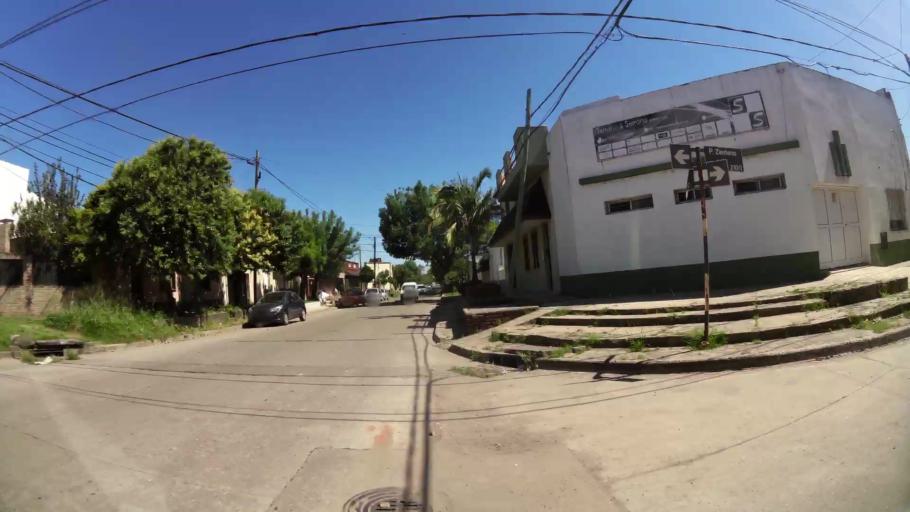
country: AR
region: Santa Fe
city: Santa Fe de la Vera Cruz
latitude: -31.6287
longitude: -60.6942
